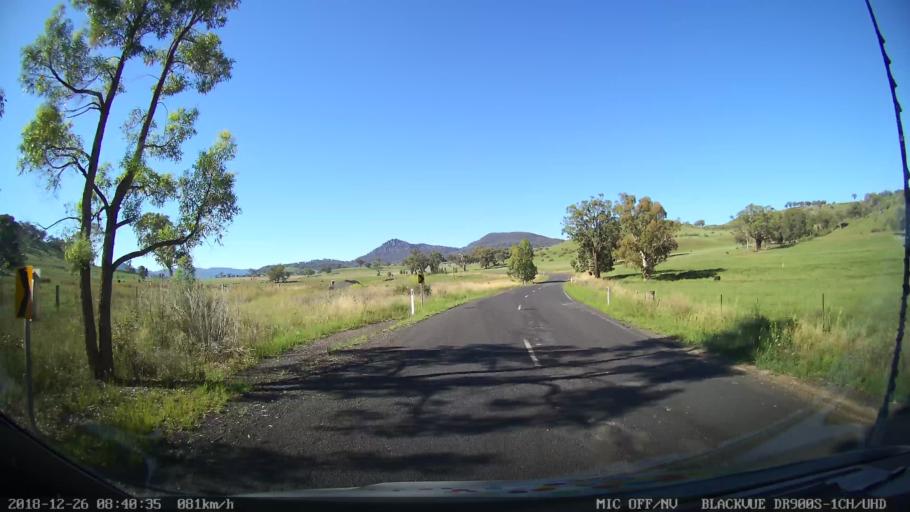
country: AU
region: New South Wales
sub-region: Mid-Western Regional
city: Kandos
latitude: -32.4686
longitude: 150.0755
